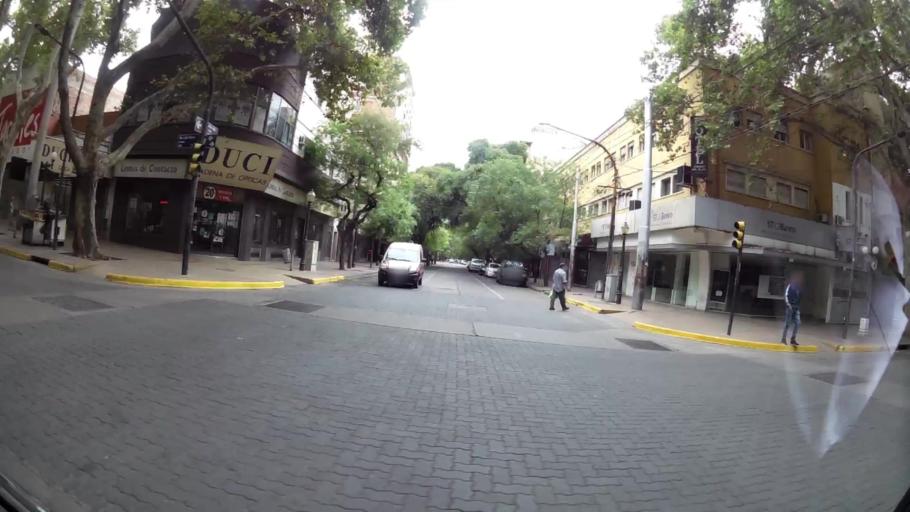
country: AR
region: Mendoza
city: Mendoza
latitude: -32.8860
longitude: -68.8393
